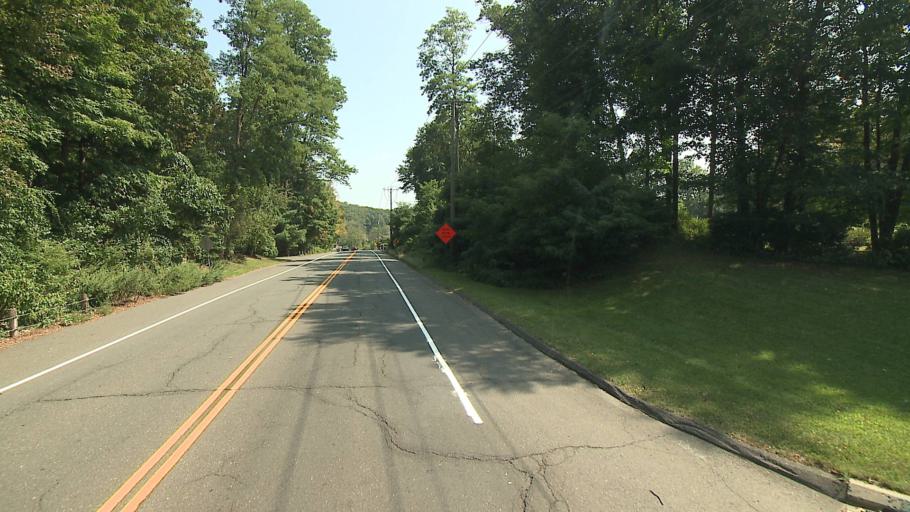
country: US
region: Connecticut
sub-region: Fairfield County
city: Georgetown
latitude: 41.2685
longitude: -73.4457
